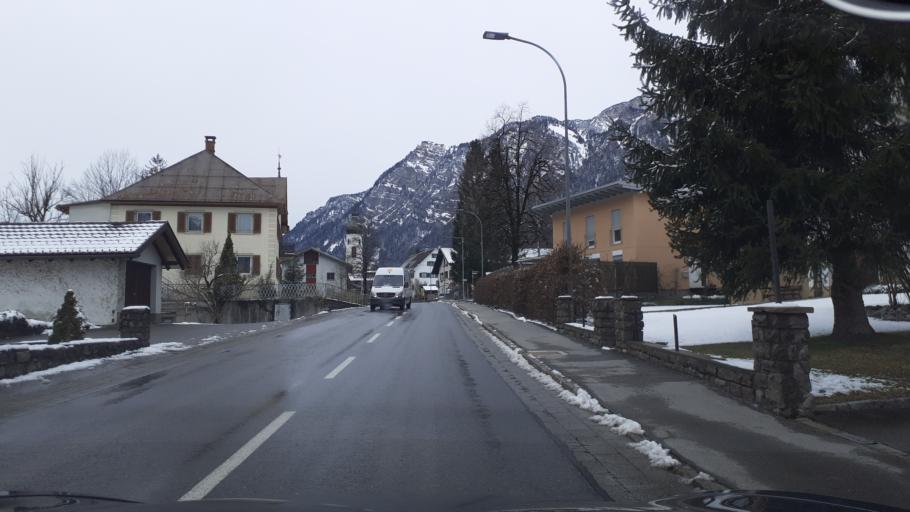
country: AT
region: Vorarlberg
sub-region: Politischer Bezirk Bludenz
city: Innerbraz
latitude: 47.1439
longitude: 9.9204
